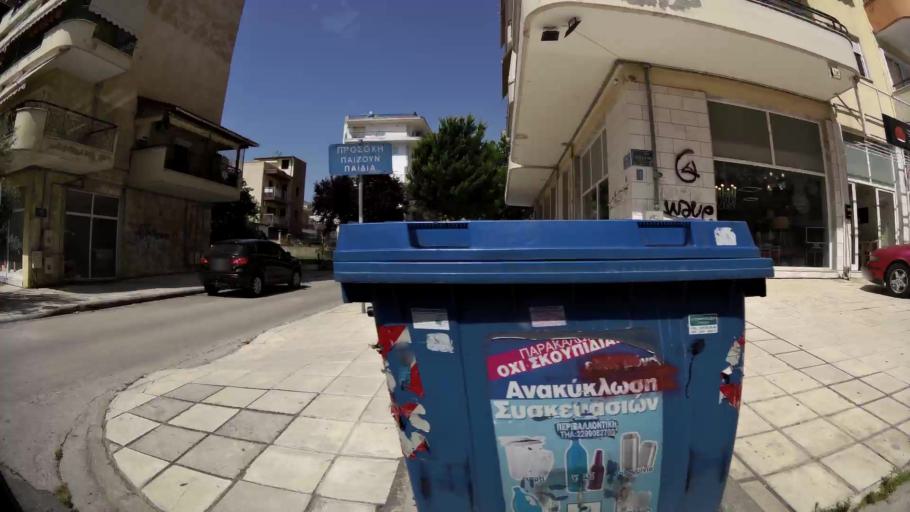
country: GR
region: Central Macedonia
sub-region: Nomos Thessalonikis
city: Evosmos
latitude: 40.6705
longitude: 22.9203
